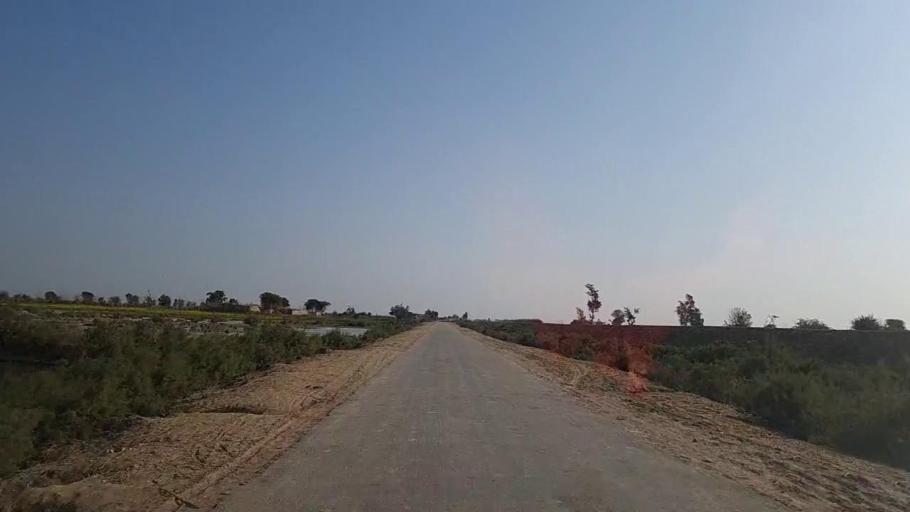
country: PK
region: Sindh
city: Sanghar
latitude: 25.9530
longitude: 69.0449
